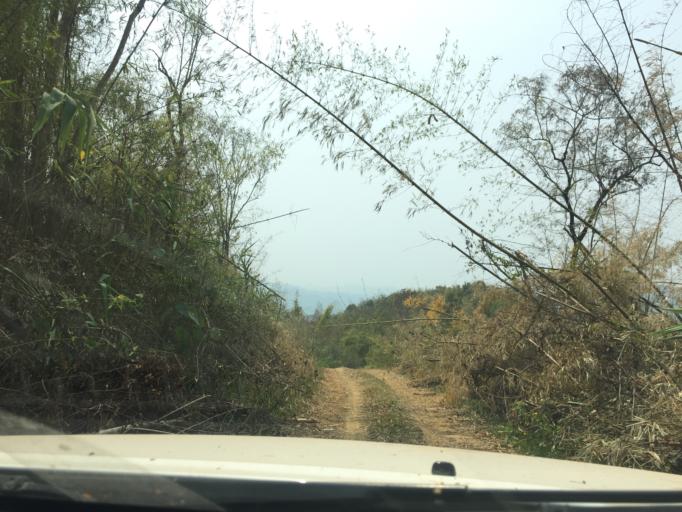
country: LA
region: Loungnamtha
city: Muang Nale
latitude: 20.6147
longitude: 101.6046
